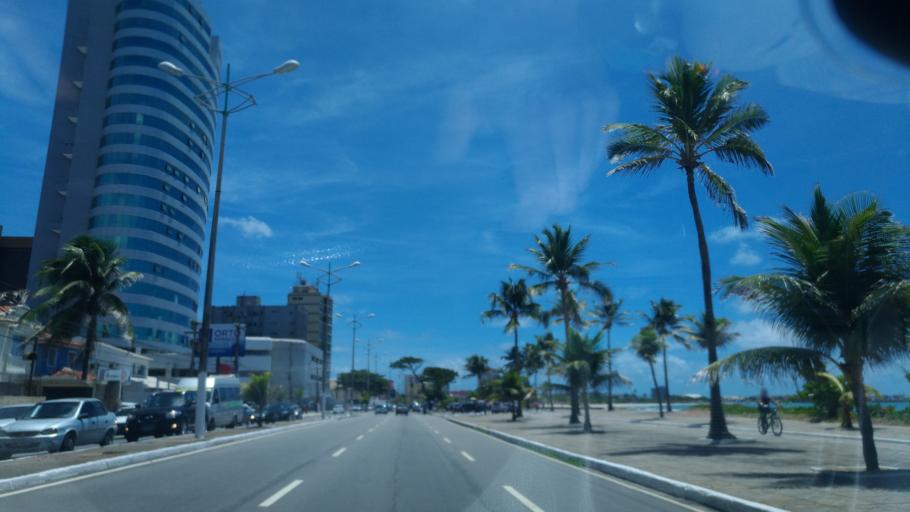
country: BR
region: Alagoas
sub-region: Maceio
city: Maceio
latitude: -9.6699
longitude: -35.7371
